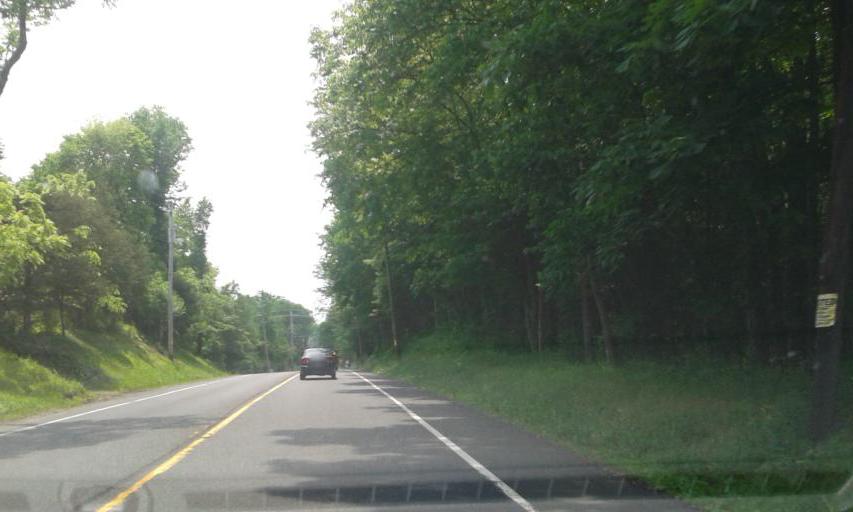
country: US
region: New Jersey
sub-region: Hunterdon County
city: Whitehouse Station
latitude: 40.6474
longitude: -74.7571
